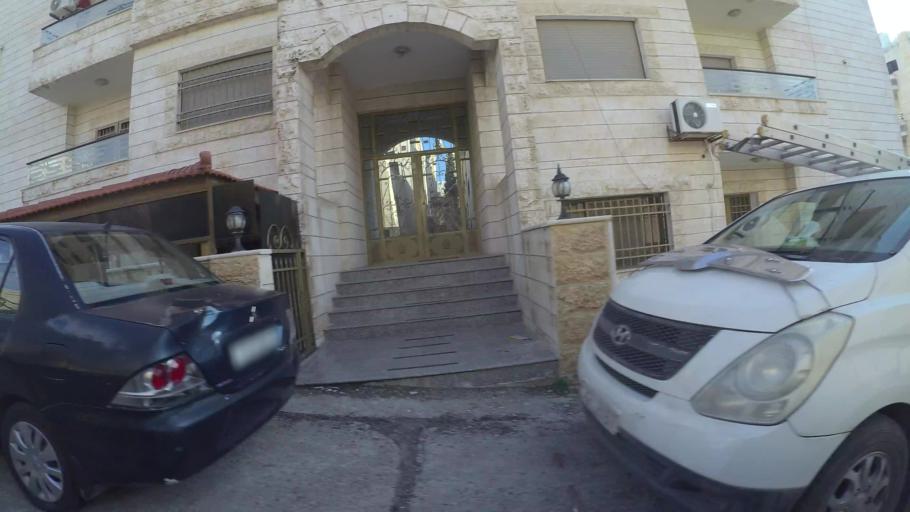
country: JO
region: Amman
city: Al Jubayhah
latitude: 31.9952
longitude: 35.8671
